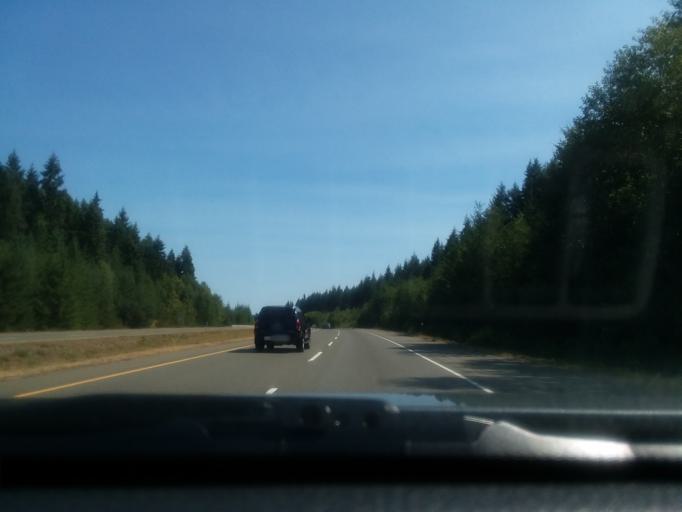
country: CA
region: British Columbia
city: Port Alberni
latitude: 49.4228
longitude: -124.7244
